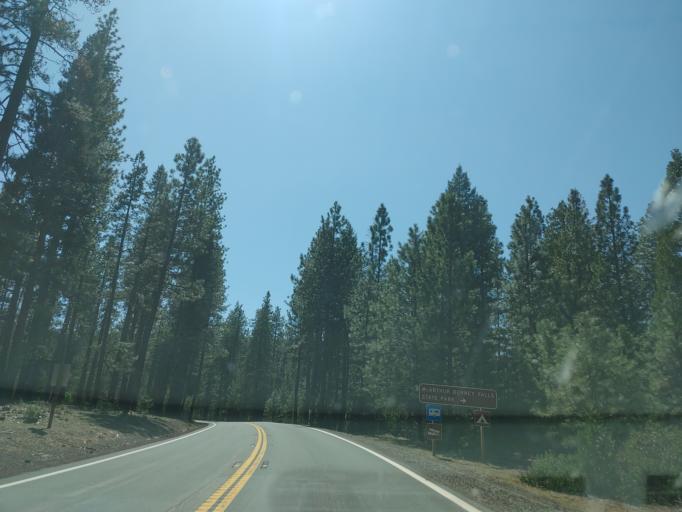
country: US
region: California
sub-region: Shasta County
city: Burney
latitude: 41.0142
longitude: -121.6485
